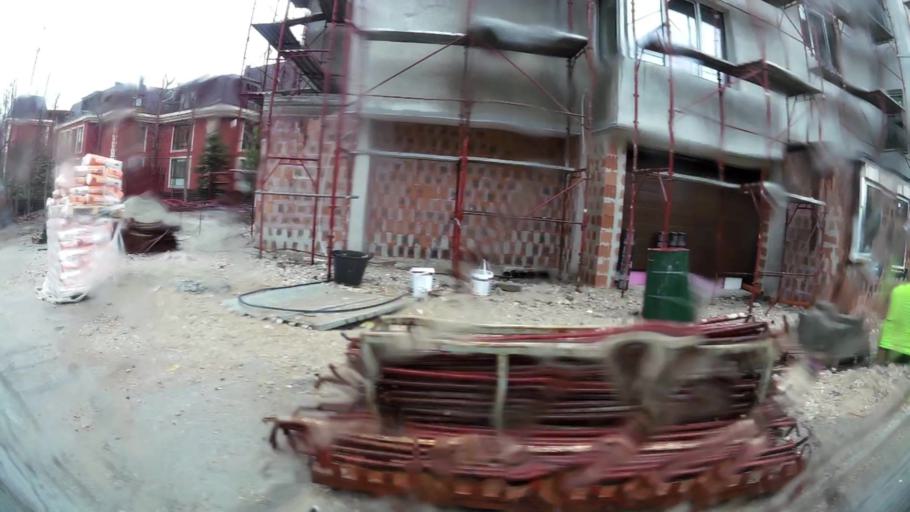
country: BG
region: Sofia-Capital
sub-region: Stolichna Obshtina
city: Sofia
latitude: 42.6420
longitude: 23.3320
